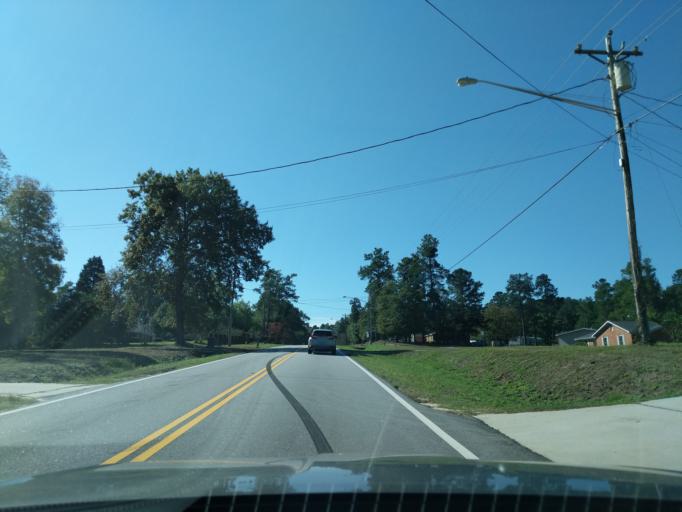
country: US
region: Georgia
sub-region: Richmond County
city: Hephzibah
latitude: 33.3308
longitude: -82.0091
